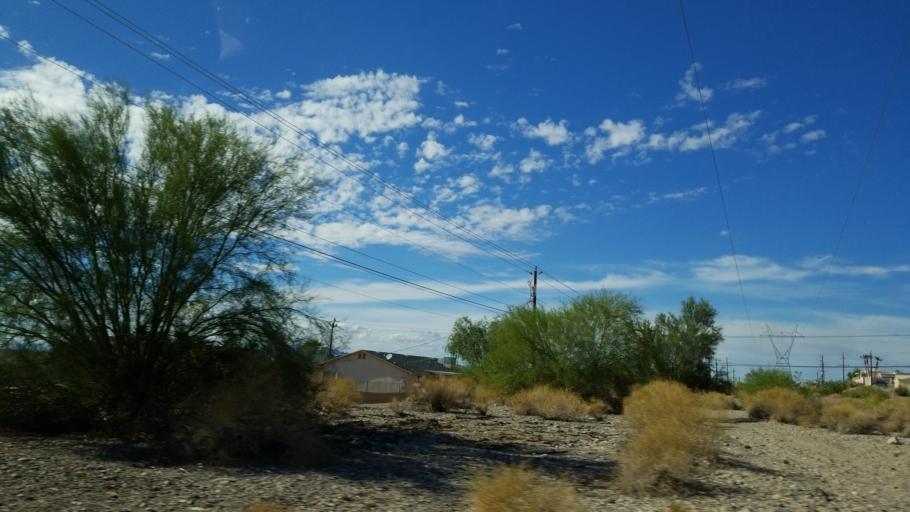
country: US
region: Arizona
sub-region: Mohave County
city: Lake Havasu City
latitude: 34.4961
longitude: -114.2887
